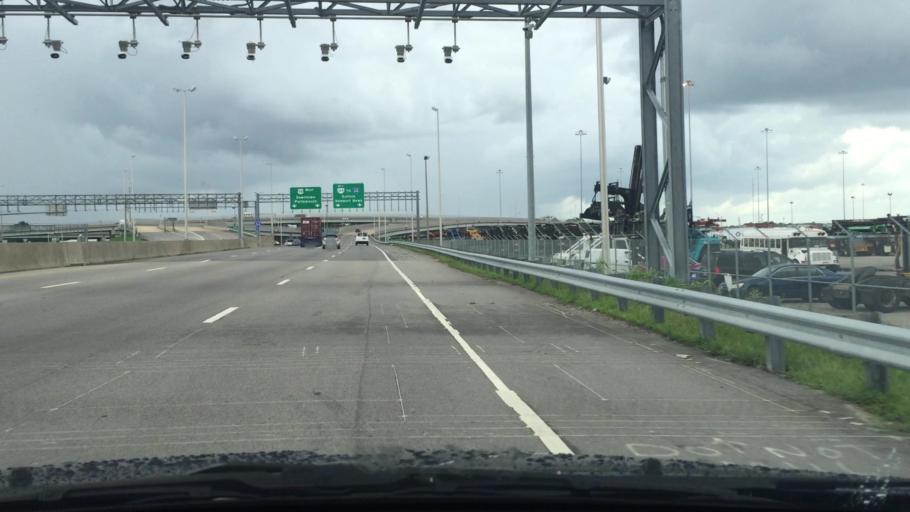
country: US
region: Virginia
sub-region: City of Portsmouth
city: Portsmouth
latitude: 36.8526
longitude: -76.3244
